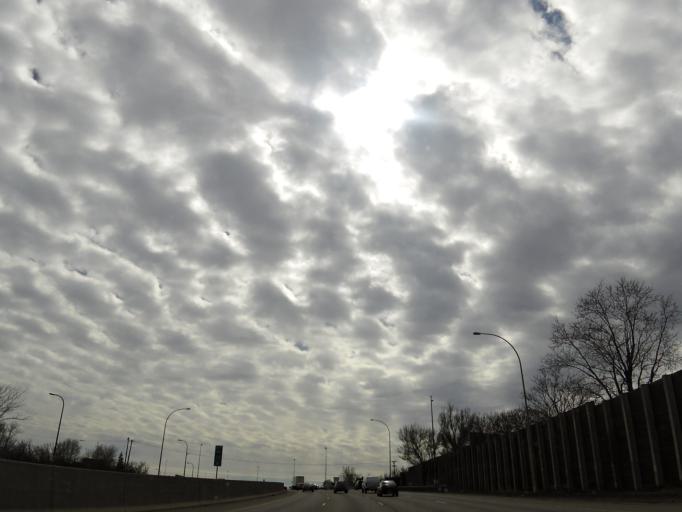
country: US
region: Minnesota
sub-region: Hennepin County
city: Minneapolis
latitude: 44.9516
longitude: -93.2737
